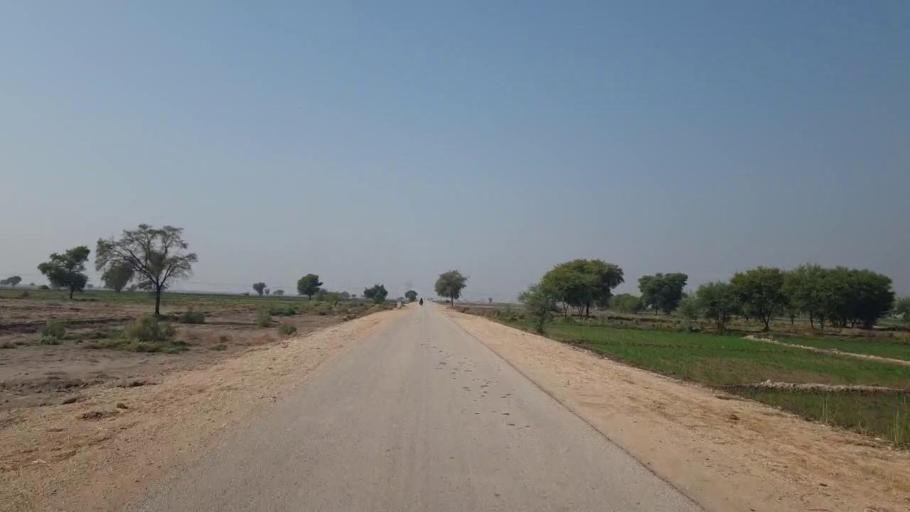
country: PK
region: Sindh
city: Sehwan
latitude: 26.4193
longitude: 67.8220
